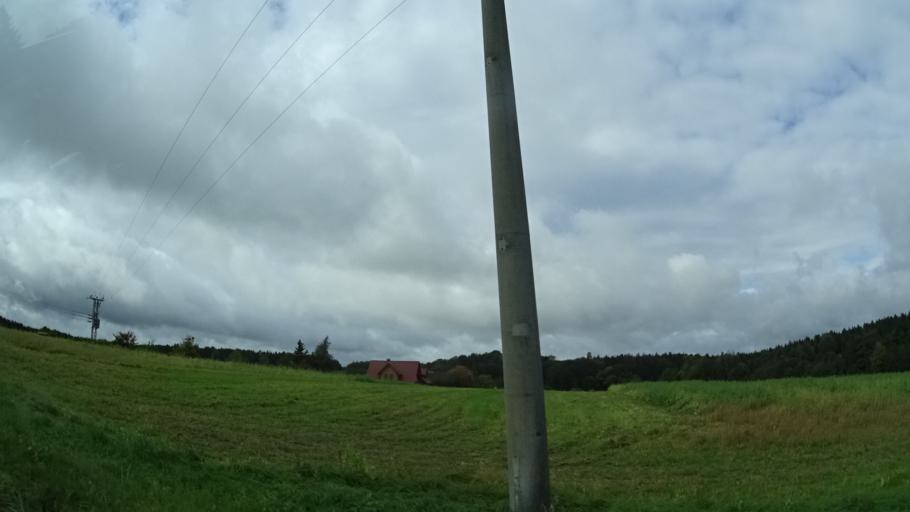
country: DE
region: Bavaria
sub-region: Upper Franconia
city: Zapfendorf
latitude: 50.0020
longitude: 10.9725
